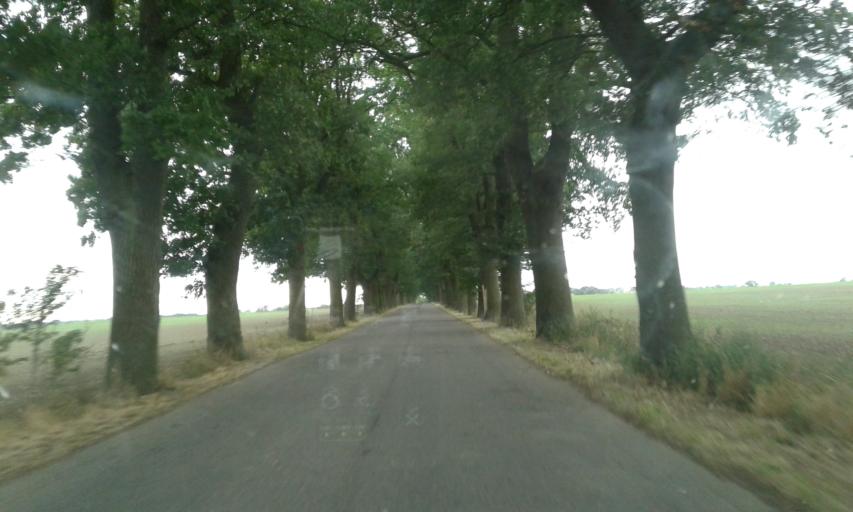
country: PL
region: West Pomeranian Voivodeship
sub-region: Powiat pyrzycki
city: Przelewice
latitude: 53.1805
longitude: 15.0399
